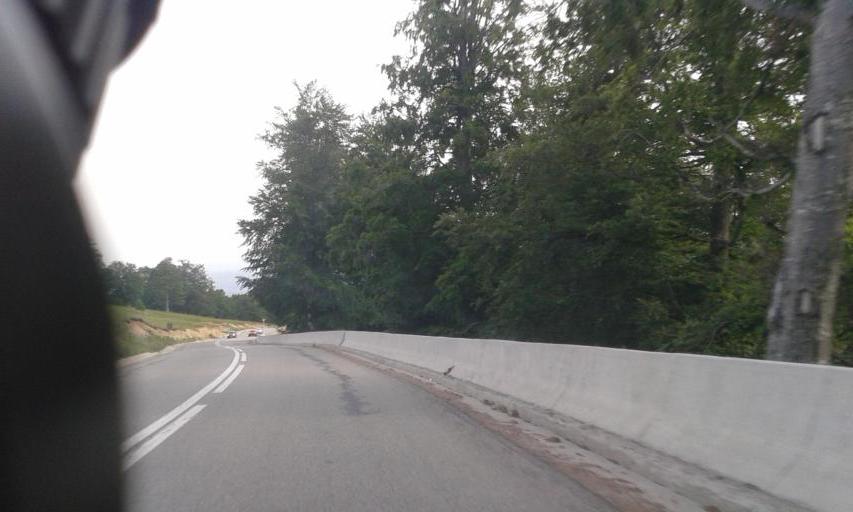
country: RO
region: Gorj
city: Novaci-Straini
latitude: 45.2421
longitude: 23.6955
